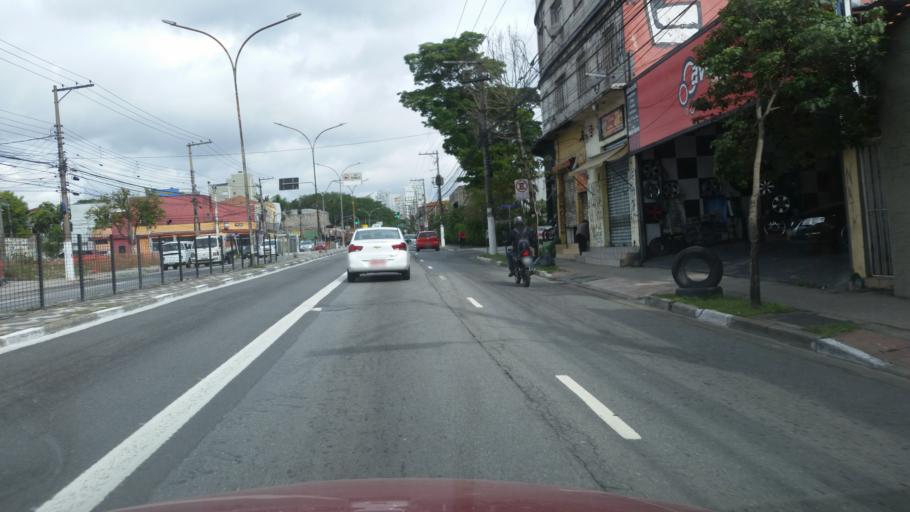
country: BR
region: Sao Paulo
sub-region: Taboao Da Serra
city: Taboao da Serra
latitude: -23.6450
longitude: -46.7160
